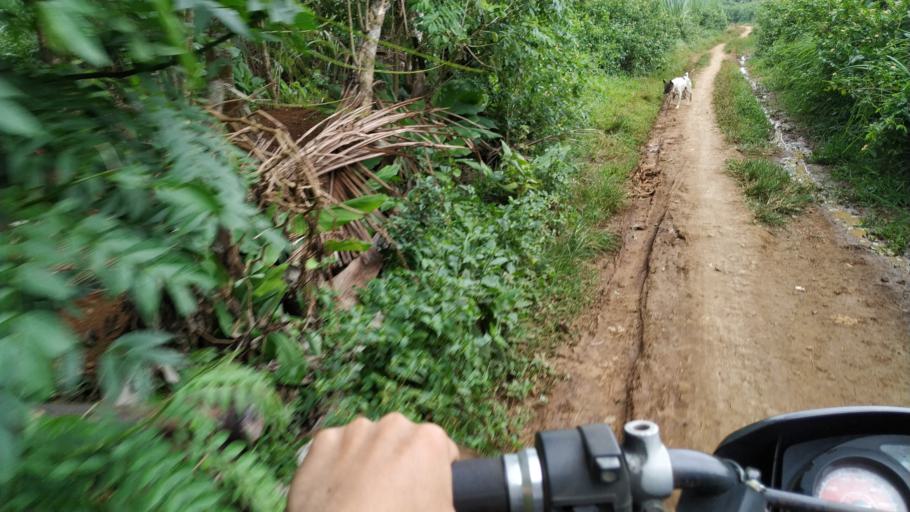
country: PH
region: Western Visayas
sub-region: Province of Negros Occidental
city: Quezon
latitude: 10.4222
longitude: 123.2398
